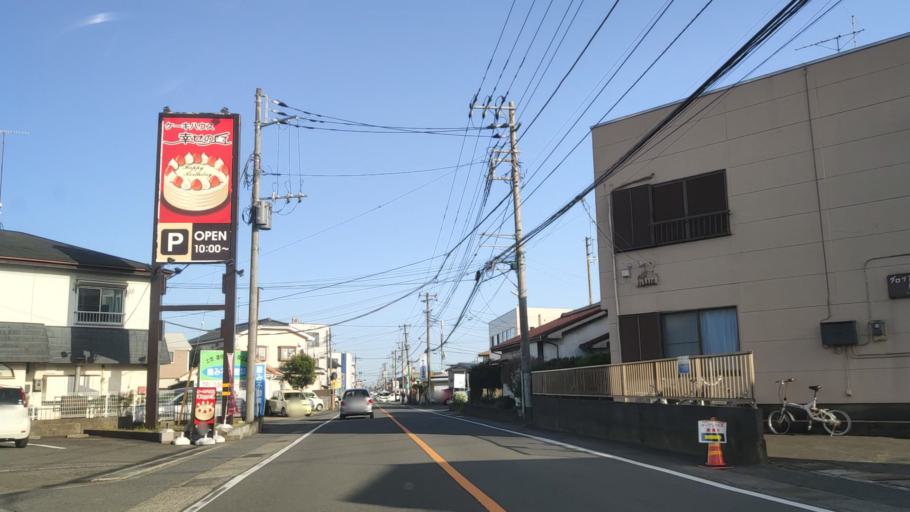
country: JP
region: Kanagawa
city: Zama
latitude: 35.5026
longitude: 139.3548
